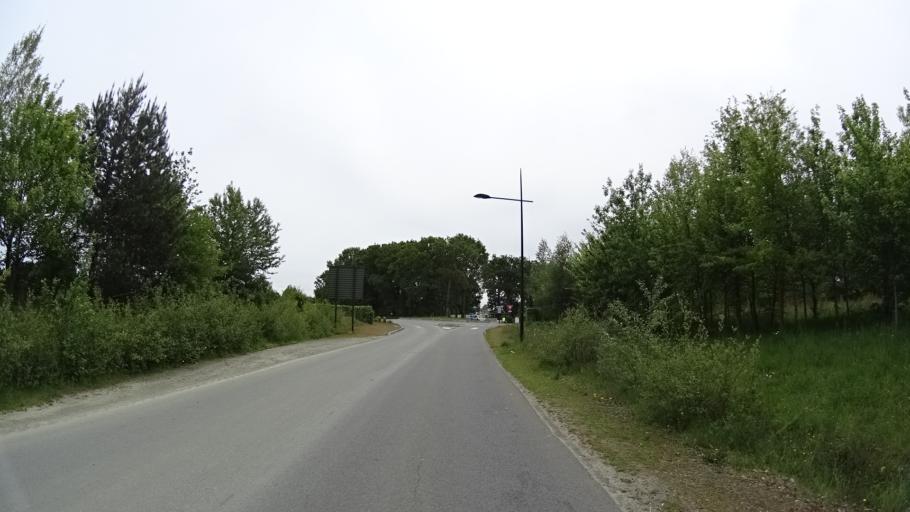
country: FR
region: Brittany
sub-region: Departement d'Ille-et-Vilaine
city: Pace
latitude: 48.1474
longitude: -1.7552
